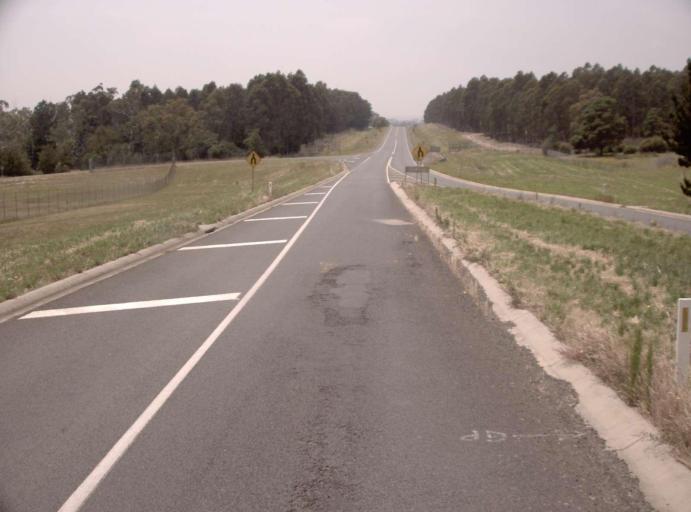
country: AU
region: Victoria
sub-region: Latrobe
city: Traralgon
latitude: -38.2527
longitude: 146.5914
